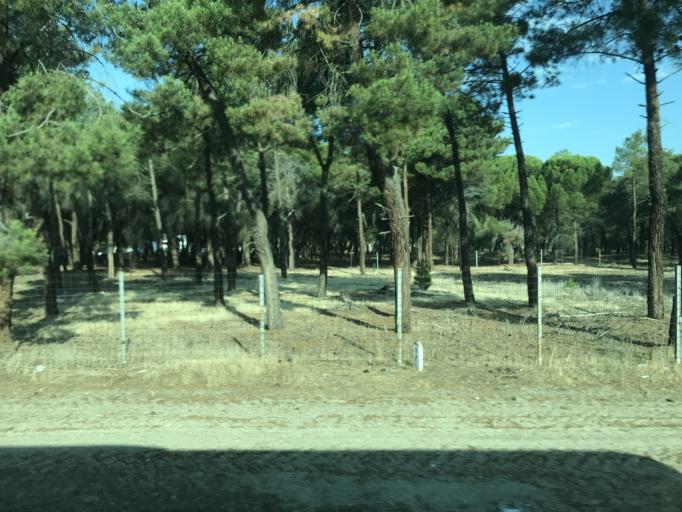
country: ES
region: Castille and Leon
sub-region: Provincia de Valladolid
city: Mojados
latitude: 41.4374
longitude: -4.6663
